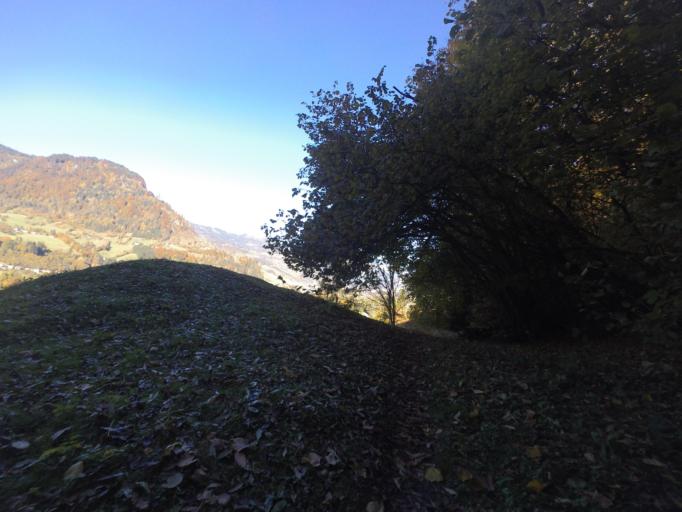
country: AT
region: Salzburg
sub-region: Politischer Bezirk Sankt Johann im Pongau
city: Schwarzach im Pongau
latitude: 47.3182
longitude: 13.1854
